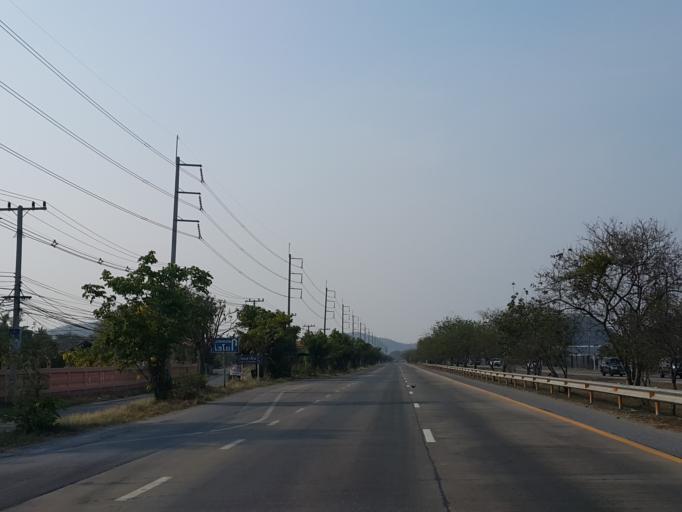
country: TH
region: Suphan Buri
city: Doembang Nangbuat
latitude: 14.8175
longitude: 100.1161
